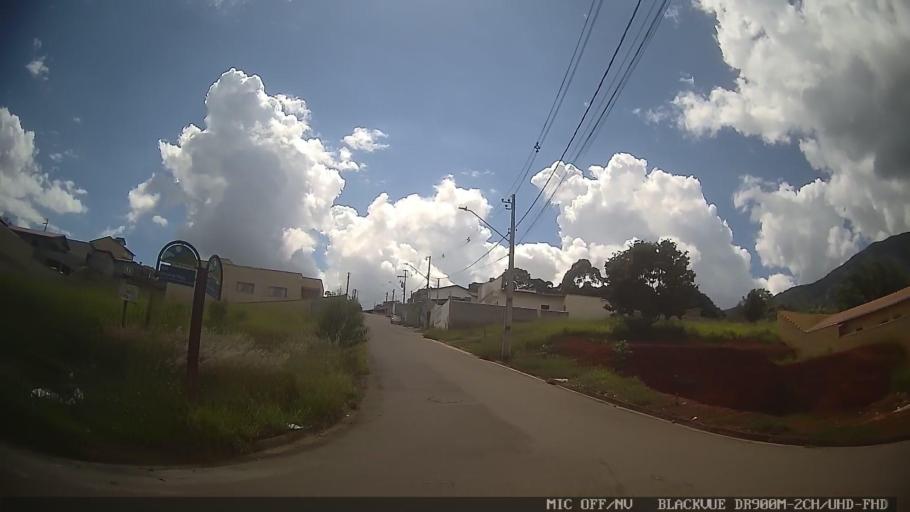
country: BR
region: Minas Gerais
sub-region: Extrema
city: Extrema
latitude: -22.8674
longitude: -46.3421
